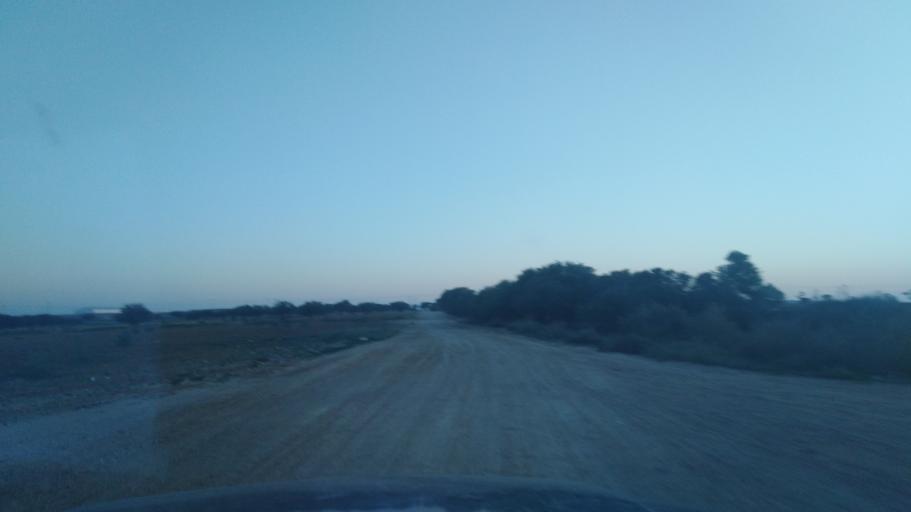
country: TN
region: Safaqis
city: Sfax
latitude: 34.7287
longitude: 10.4462
